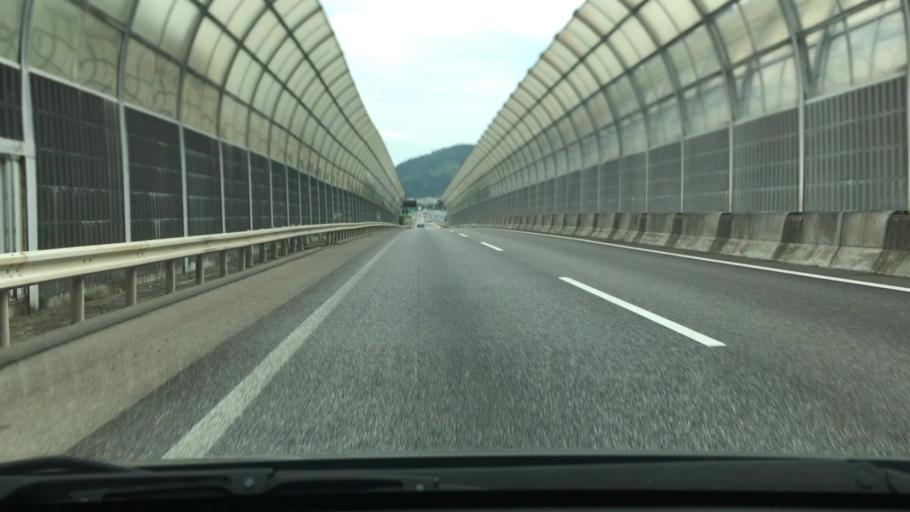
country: JP
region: Yamaguchi
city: Otake
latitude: 34.2510
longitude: 132.2205
